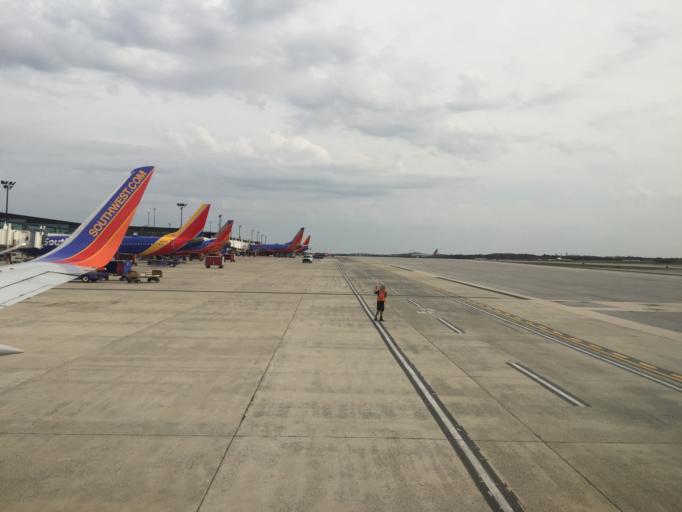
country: US
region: Maryland
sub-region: Anne Arundel County
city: Linthicum
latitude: 39.1793
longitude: -76.6727
